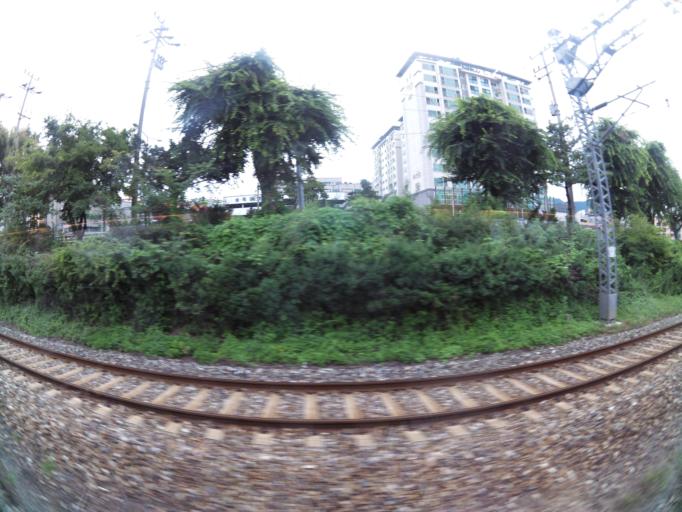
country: KR
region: Gyeonggi-do
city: Anyang-si
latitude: 37.3612
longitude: 126.9485
